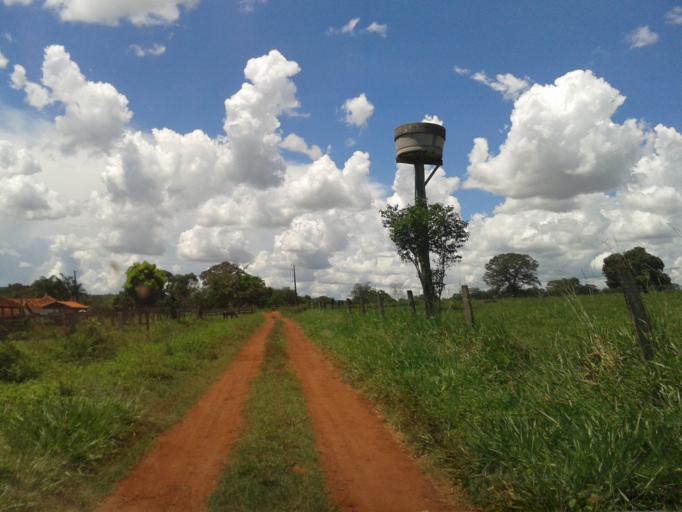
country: BR
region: Minas Gerais
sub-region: Santa Vitoria
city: Santa Vitoria
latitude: -18.7955
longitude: -49.8381
